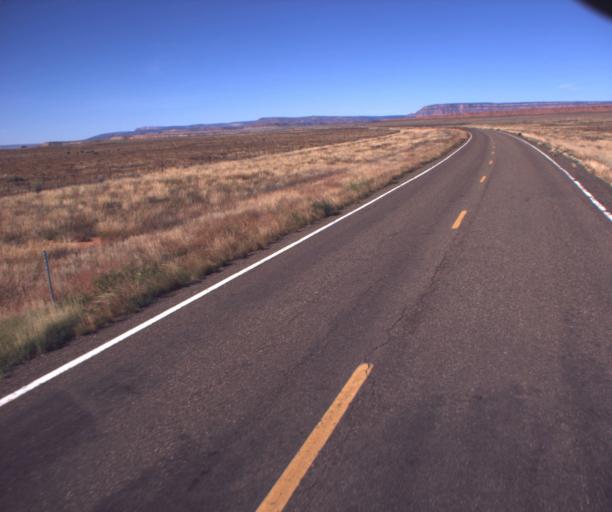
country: US
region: Arizona
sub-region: Coconino County
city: Fredonia
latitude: 36.9205
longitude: -112.4375
